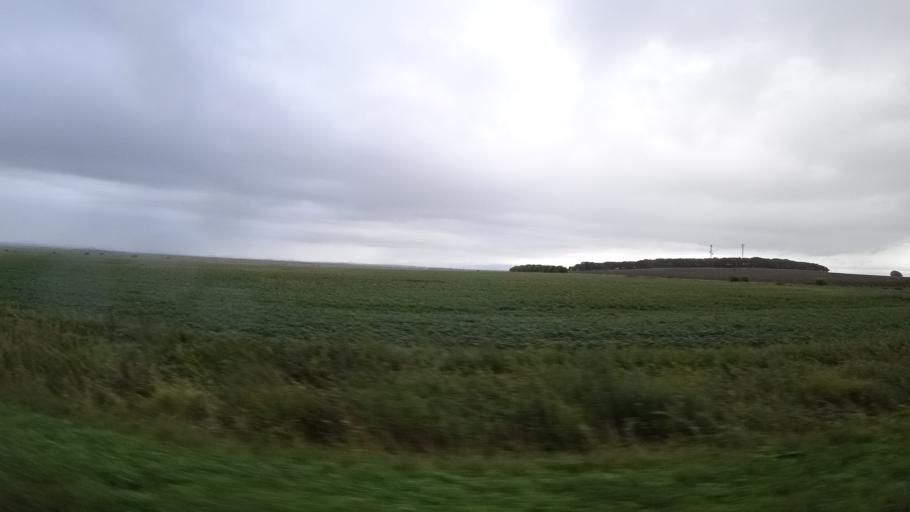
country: RU
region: Primorskiy
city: Chernigovka
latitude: 44.3736
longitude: 132.5298
